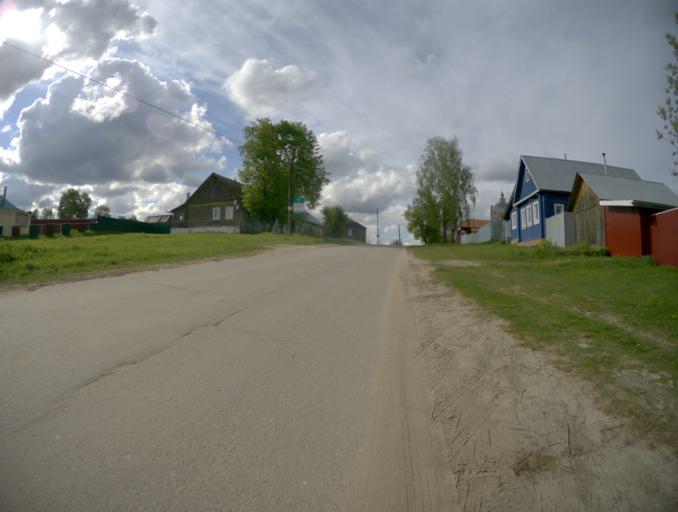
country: RU
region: Rjazan
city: Gus'-Zheleznyy
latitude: 55.0533
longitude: 41.1606
